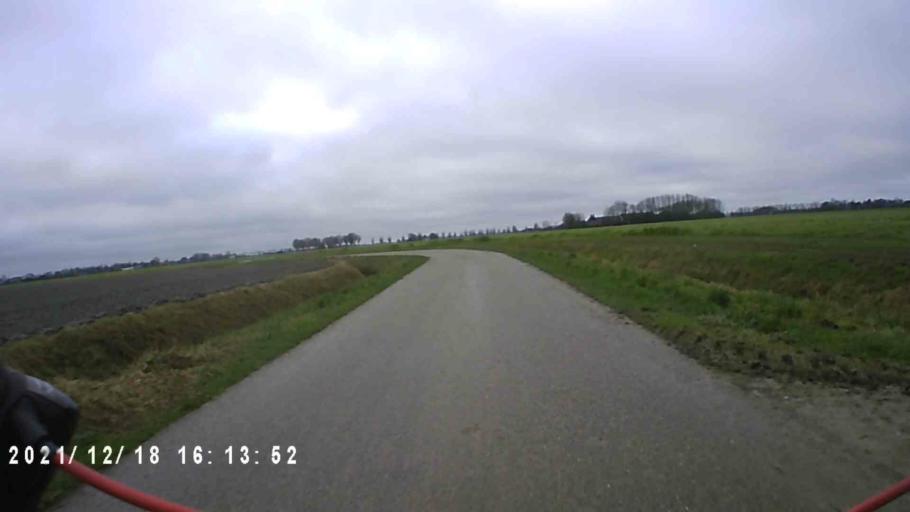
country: NL
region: Friesland
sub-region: Gemeente Dongeradeel
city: Anjum
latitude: 53.3690
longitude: 6.0682
